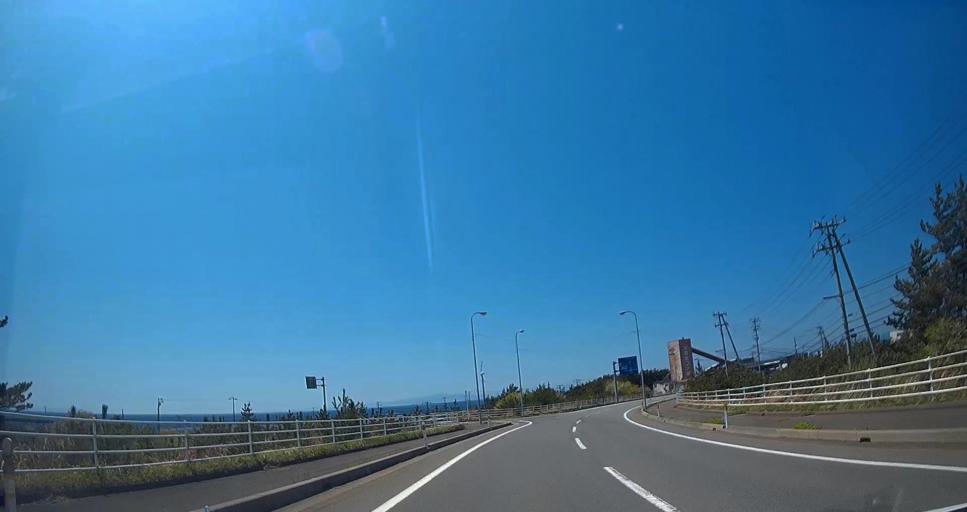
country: JP
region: Hokkaido
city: Hakodate
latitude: 41.5204
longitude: 140.9089
